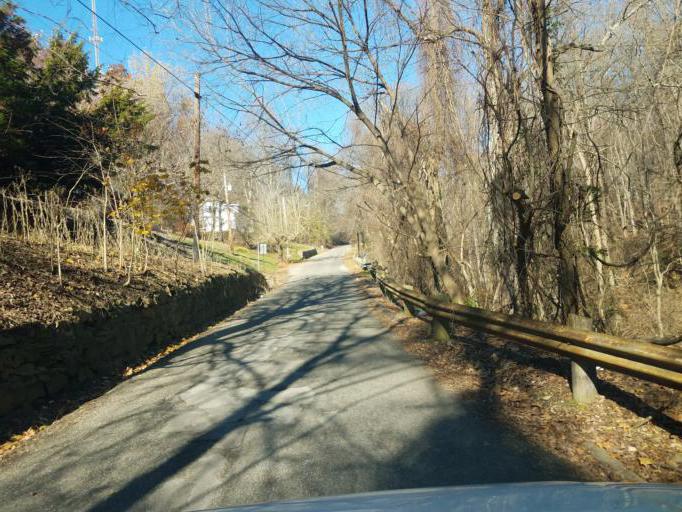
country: US
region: Ohio
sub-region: Scioto County
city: New Boston
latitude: 38.7509
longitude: -82.9632
